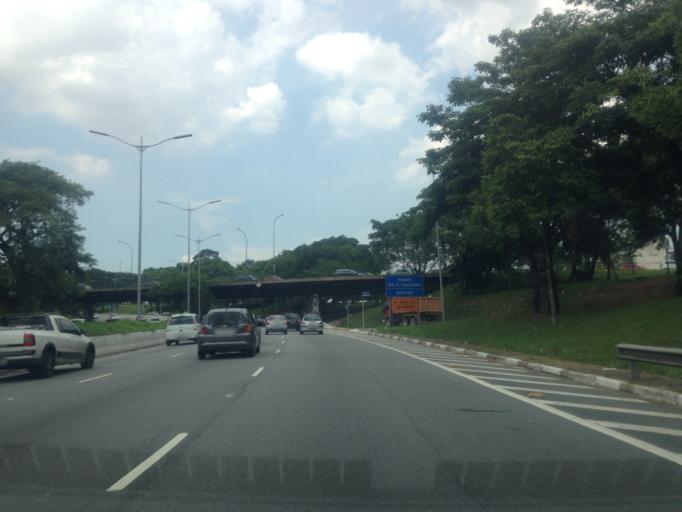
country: BR
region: Sao Paulo
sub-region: Sao Paulo
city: Sao Paulo
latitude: -23.5836
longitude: -46.6530
